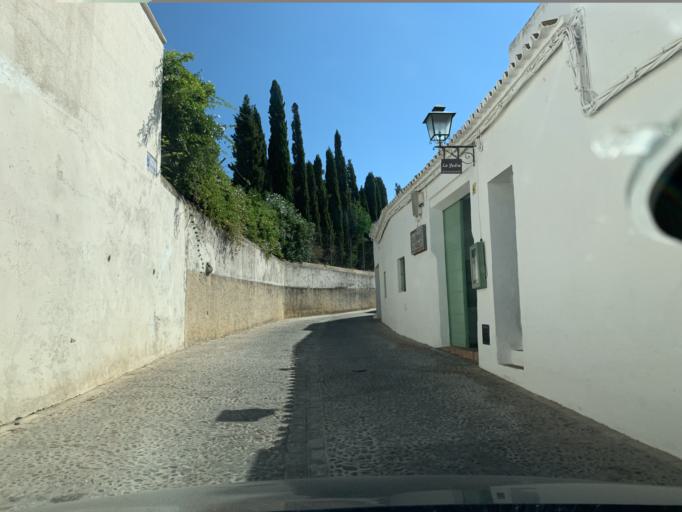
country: ES
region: Andalusia
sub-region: Provincia de Sevilla
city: Carmona
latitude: 37.4726
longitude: -5.6347
